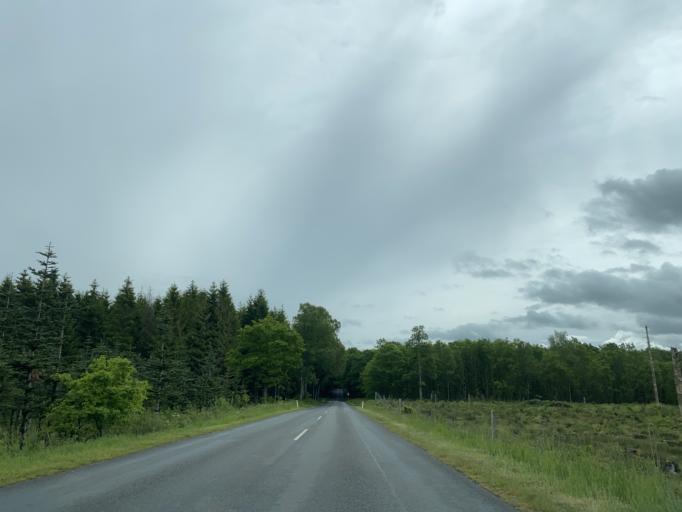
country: DK
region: Central Jutland
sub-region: Favrskov Kommune
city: Hammel
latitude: 56.2605
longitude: 9.9384
